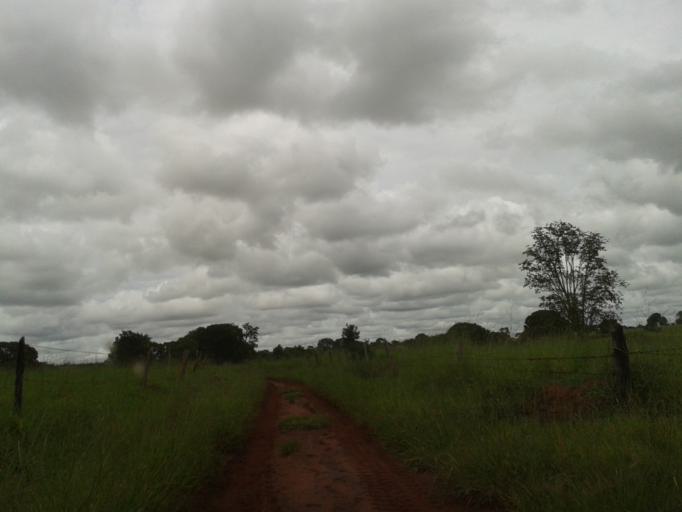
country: BR
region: Minas Gerais
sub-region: Capinopolis
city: Capinopolis
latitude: -18.7848
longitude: -49.7860
